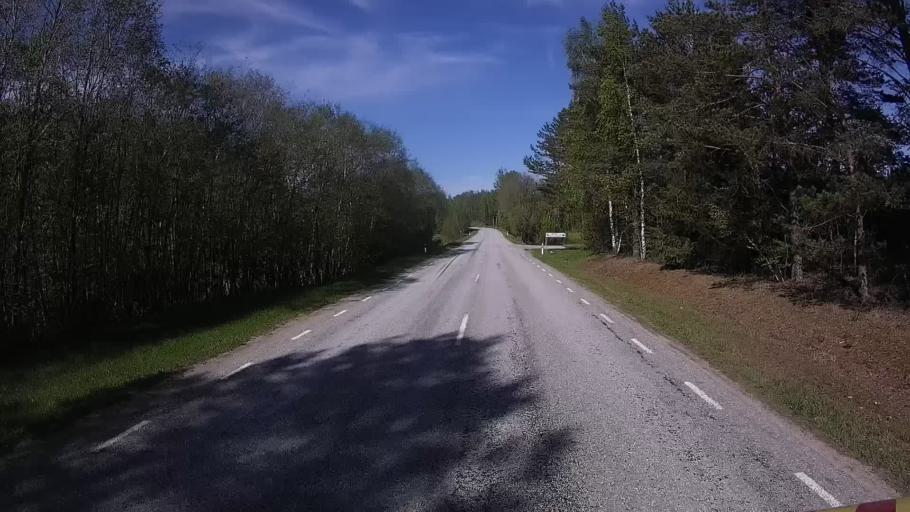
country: EE
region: Vorumaa
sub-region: Antsla vald
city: Vana-Antsla
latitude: 57.9919
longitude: 26.4897
